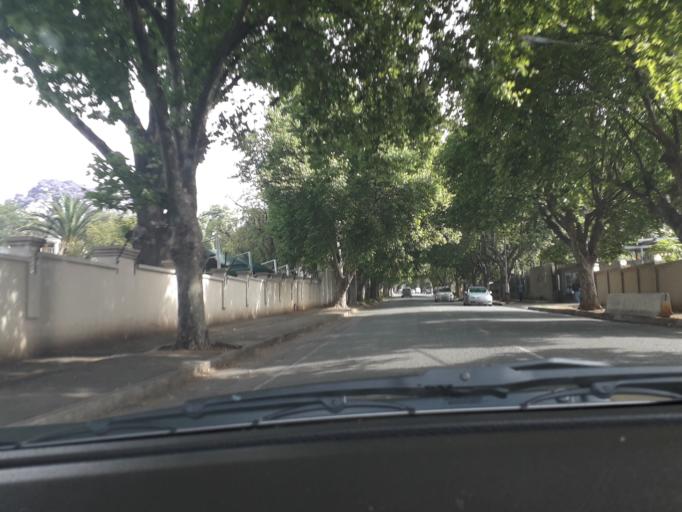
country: ZA
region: Gauteng
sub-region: City of Johannesburg Metropolitan Municipality
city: Johannesburg
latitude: -26.1636
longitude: 28.0577
